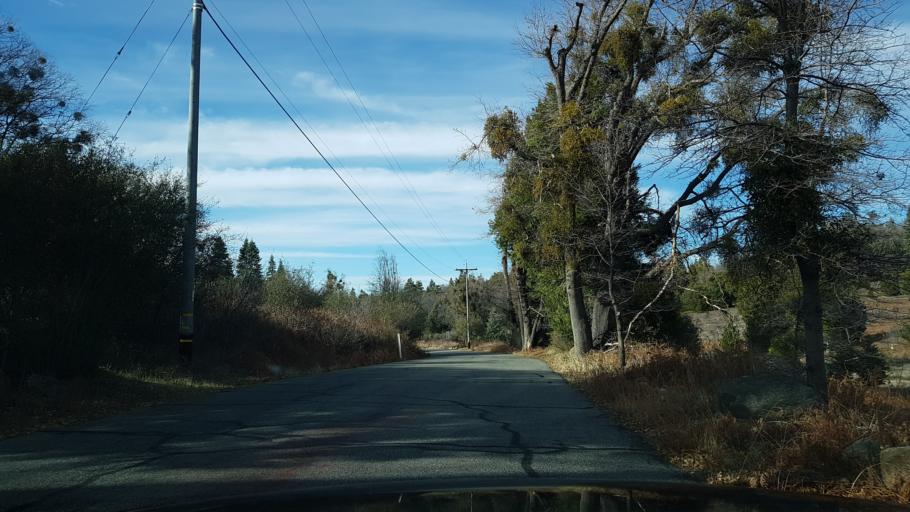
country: US
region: California
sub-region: Riverside County
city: Aguanga
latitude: 33.3297
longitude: -116.9014
